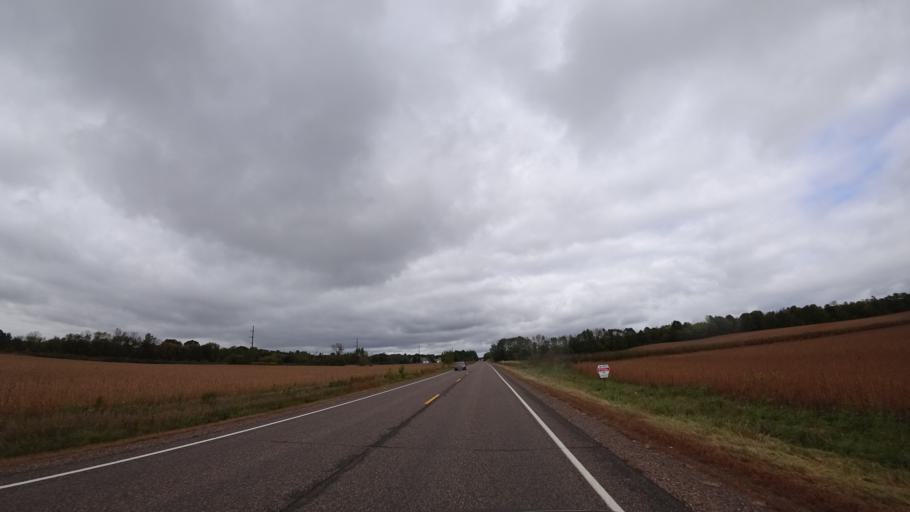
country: US
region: Wisconsin
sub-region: Chippewa County
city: Lake Wissota
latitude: 45.0142
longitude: -91.2867
